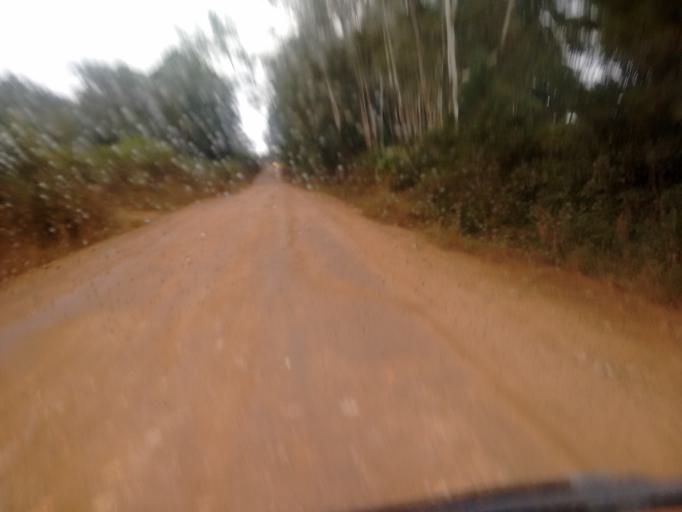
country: BR
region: Rio Grande do Sul
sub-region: Camaqua
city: Camaqua
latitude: -30.8094
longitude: -51.8257
